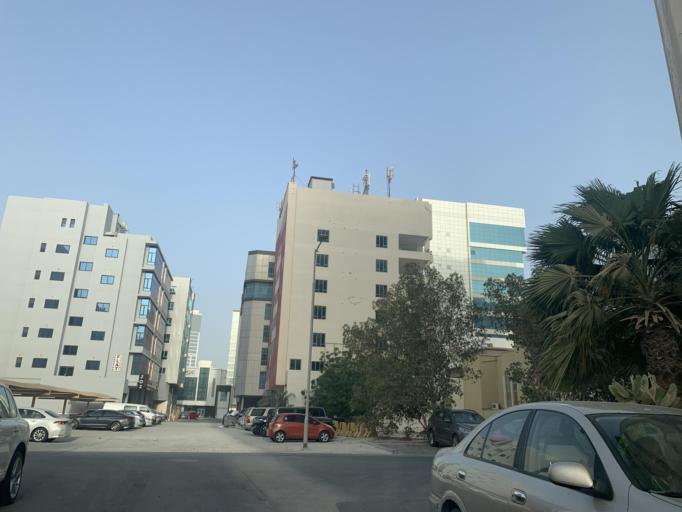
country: BH
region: Manama
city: Jidd Hafs
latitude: 26.2379
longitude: 50.5309
